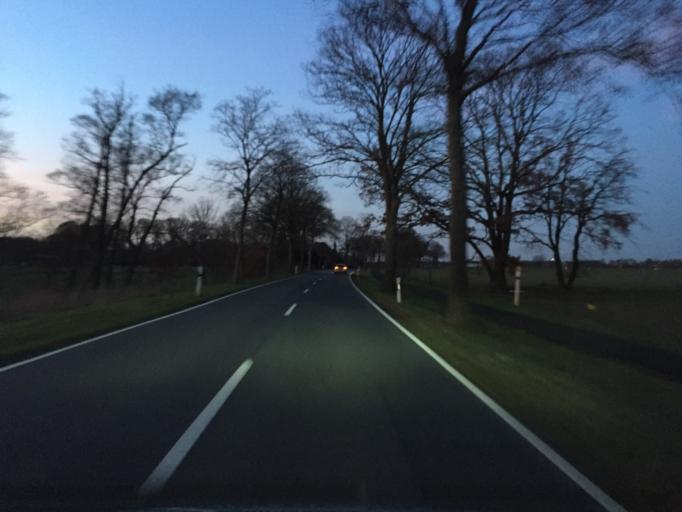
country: DE
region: Lower Saxony
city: Borstel
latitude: 52.6028
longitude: 8.9408
